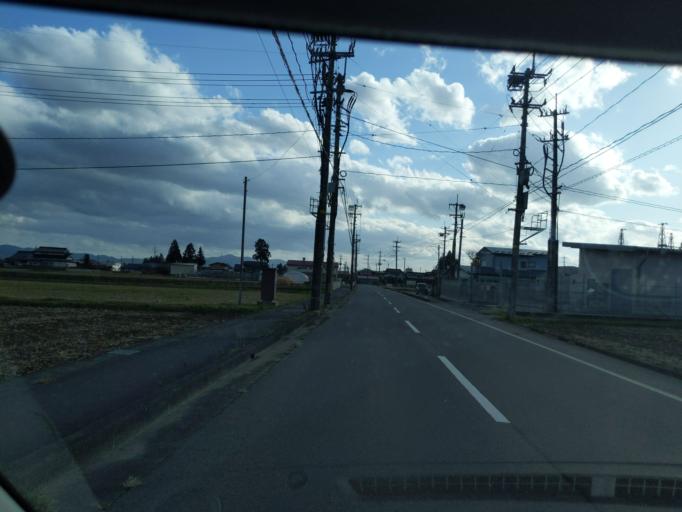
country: JP
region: Iwate
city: Mizusawa
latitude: 39.1472
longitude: 141.1591
